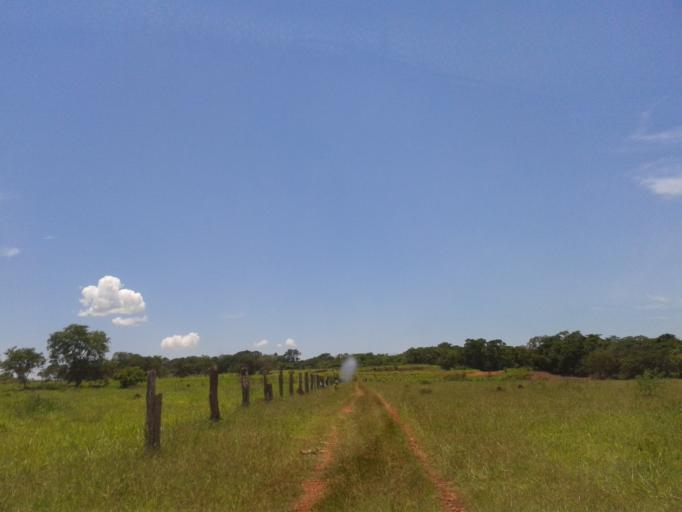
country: BR
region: Minas Gerais
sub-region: Santa Vitoria
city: Santa Vitoria
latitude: -19.1380
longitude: -50.5738
